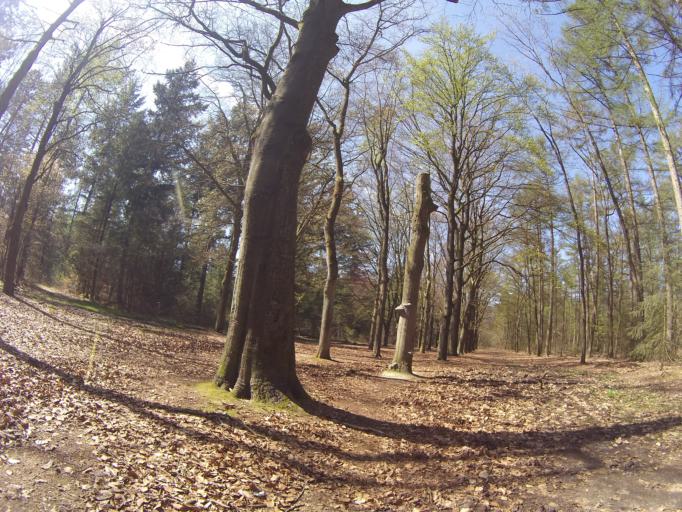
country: NL
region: Utrecht
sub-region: Gemeente Utrechtse Heuvelrug
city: Driebergen-Rijsenburg
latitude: 52.0850
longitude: 5.3099
